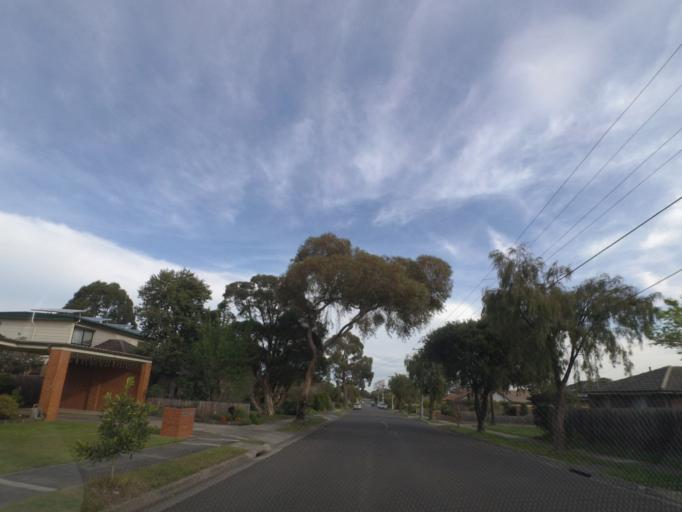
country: AU
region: Victoria
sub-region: Knox
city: Knoxfield
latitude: -37.8923
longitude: 145.2405
